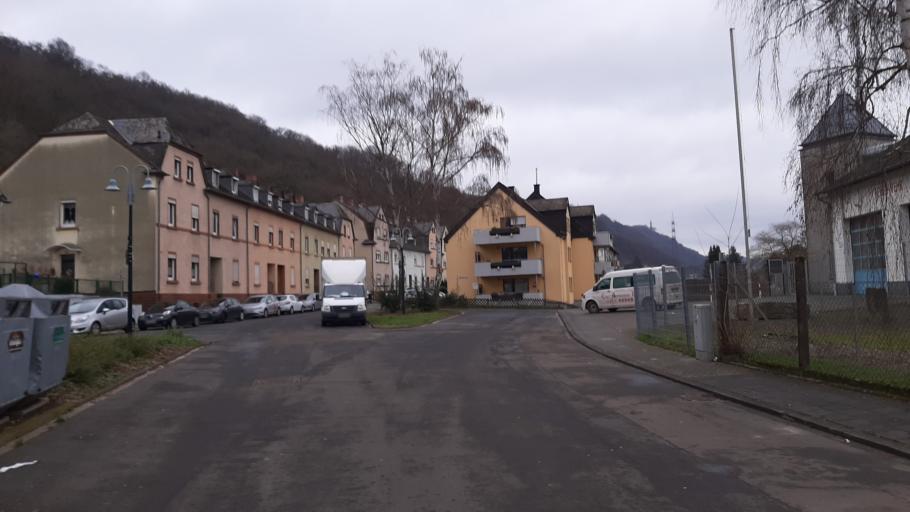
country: DE
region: Rheinland-Pfalz
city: Trier
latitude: 49.7439
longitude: 6.6098
